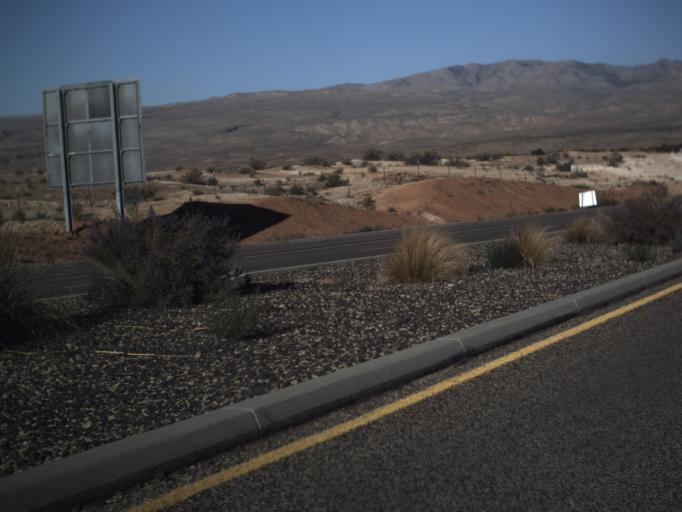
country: US
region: Utah
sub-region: Washington County
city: Saint George
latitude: 37.0287
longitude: -113.6071
